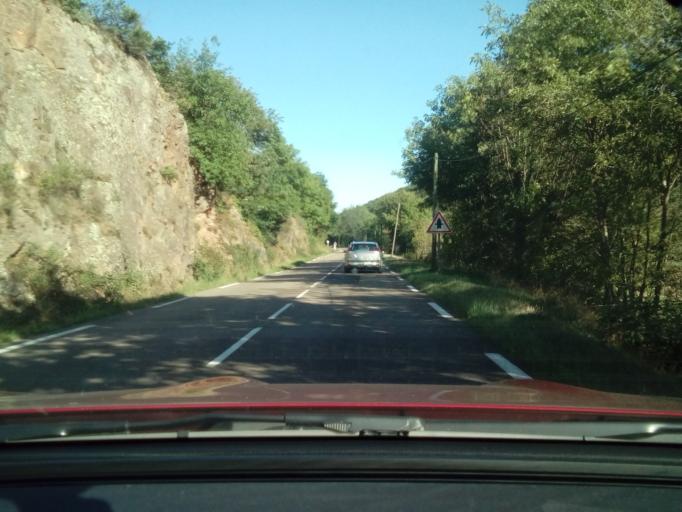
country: FR
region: Rhone-Alpes
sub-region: Departement du Rhone
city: Saint-Verand
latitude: 45.9036
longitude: 4.5326
